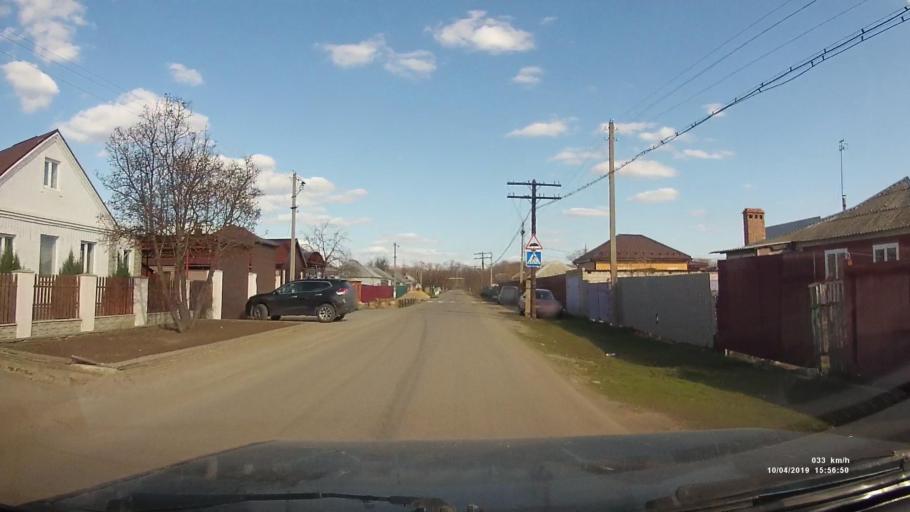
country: RU
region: Rostov
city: Masalovka
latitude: 48.4109
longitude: 40.2721
